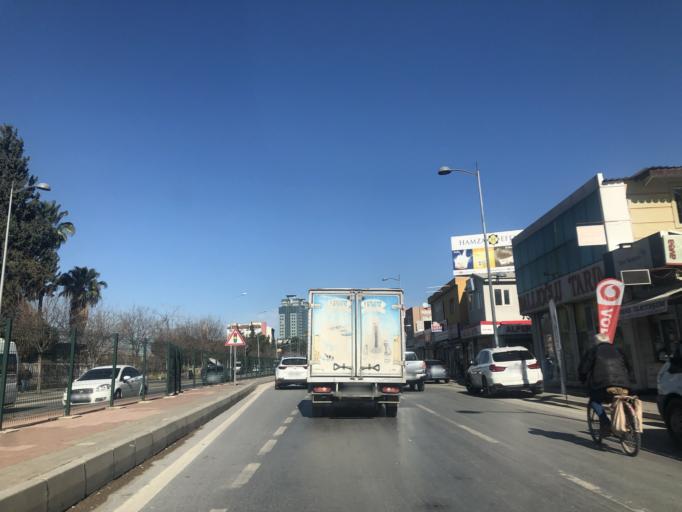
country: TR
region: Adana
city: Adana
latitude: 36.9820
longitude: 35.3382
